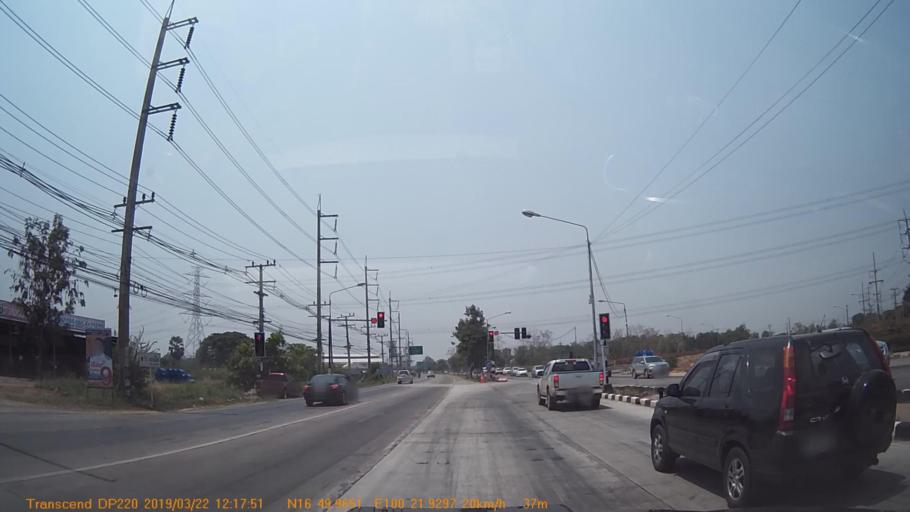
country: TH
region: Phitsanulok
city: Wang Thong
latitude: 16.8327
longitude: 100.3654
